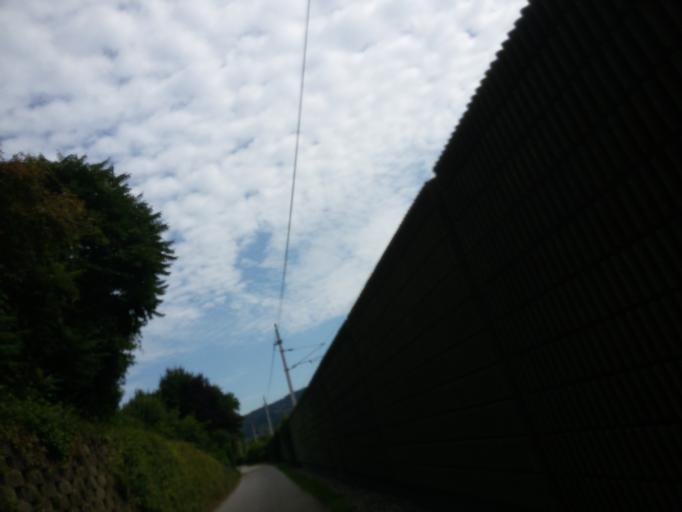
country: AT
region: Carinthia
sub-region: Politischer Bezirk Klagenfurt Land
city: Maria Worth
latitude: 46.6239
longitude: 14.1799
